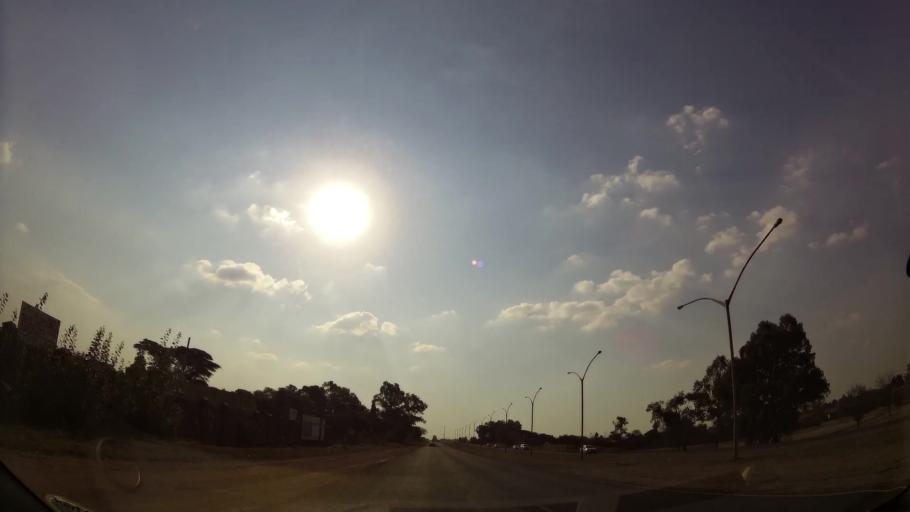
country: ZA
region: Gauteng
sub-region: Ekurhuleni Metropolitan Municipality
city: Benoni
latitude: -26.1330
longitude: 28.2907
